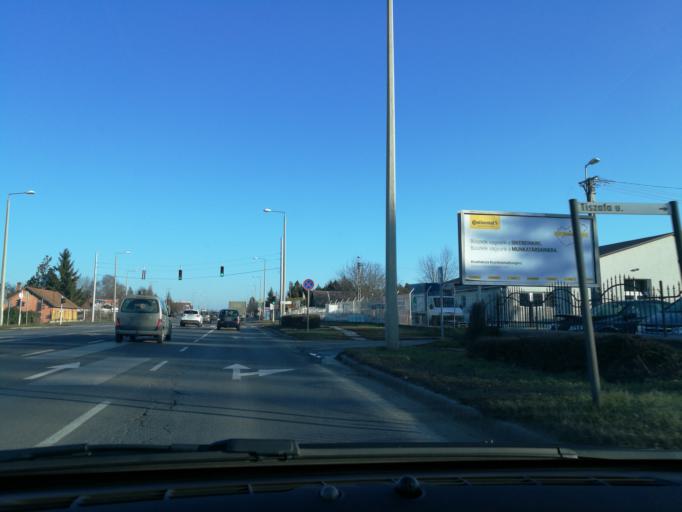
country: HU
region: Szabolcs-Szatmar-Bereg
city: Nyiregyhaza
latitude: 47.9511
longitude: 21.7593
